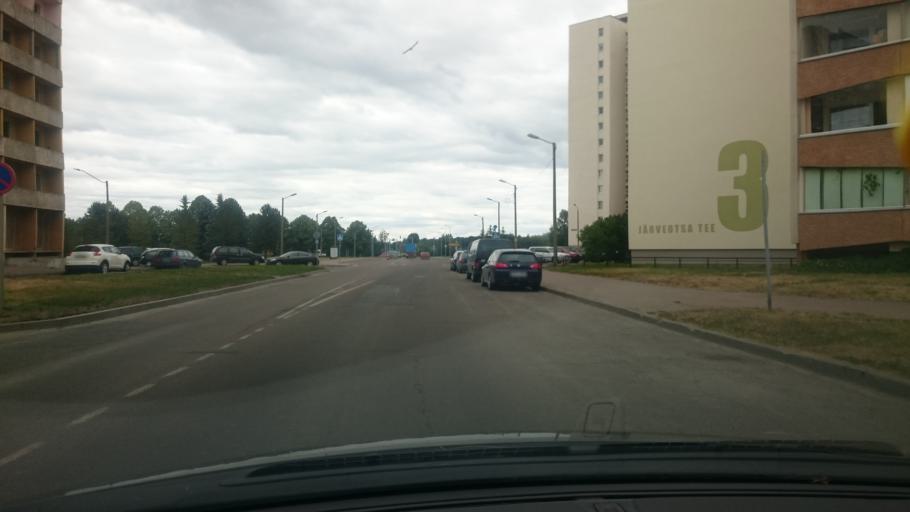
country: EE
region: Harju
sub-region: Saue vald
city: Laagri
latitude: 59.4081
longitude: 24.6331
